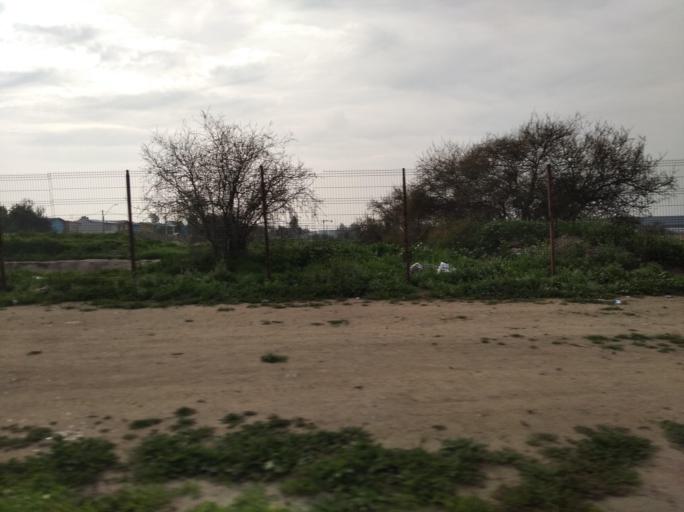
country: CL
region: Santiago Metropolitan
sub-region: Provincia de Chacabuco
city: Lampa
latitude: -33.2928
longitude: -70.8817
